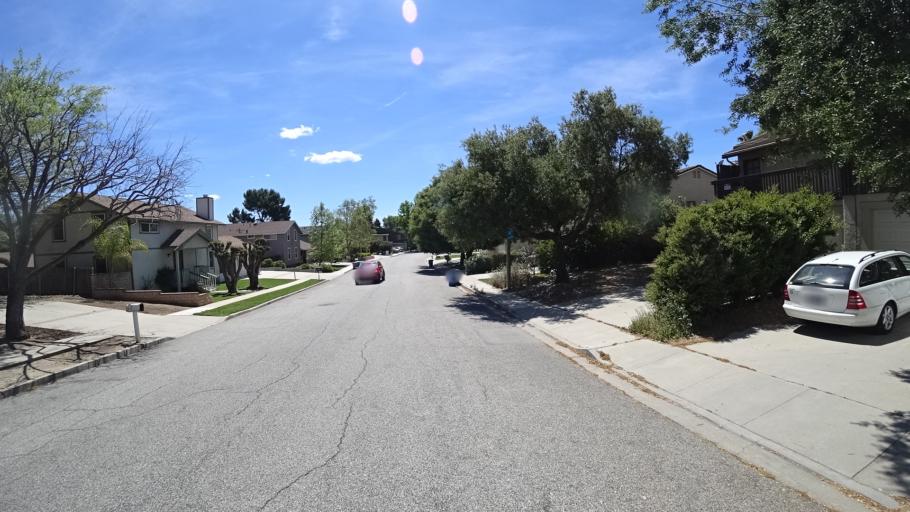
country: US
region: California
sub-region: Ventura County
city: Thousand Oaks
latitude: 34.2158
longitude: -118.8656
